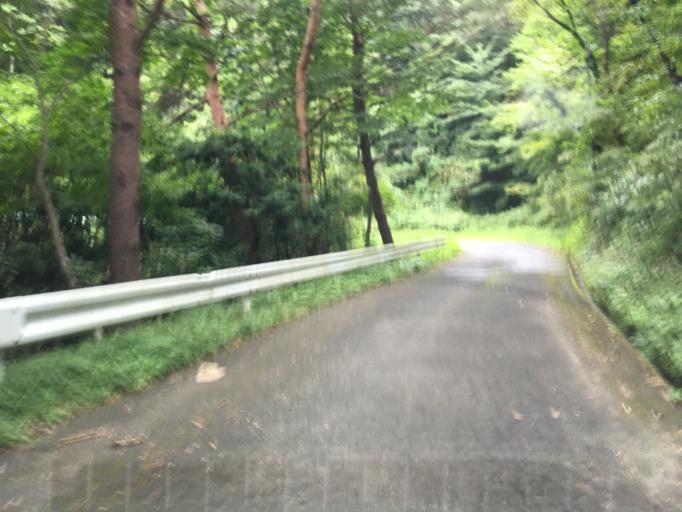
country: JP
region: Fukushima
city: Fukushima-shi
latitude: 37.8110
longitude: 140.3517
